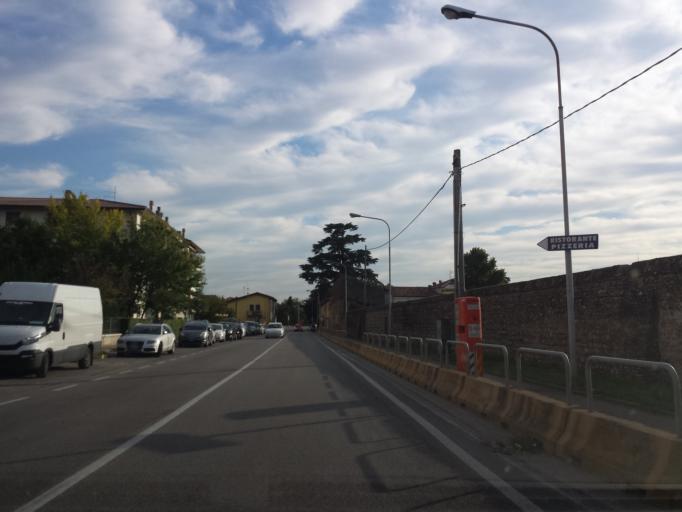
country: IT
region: Veneto
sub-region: Provincia di Verona
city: Isola della Scala
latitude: 45.2768
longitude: 10.9993
